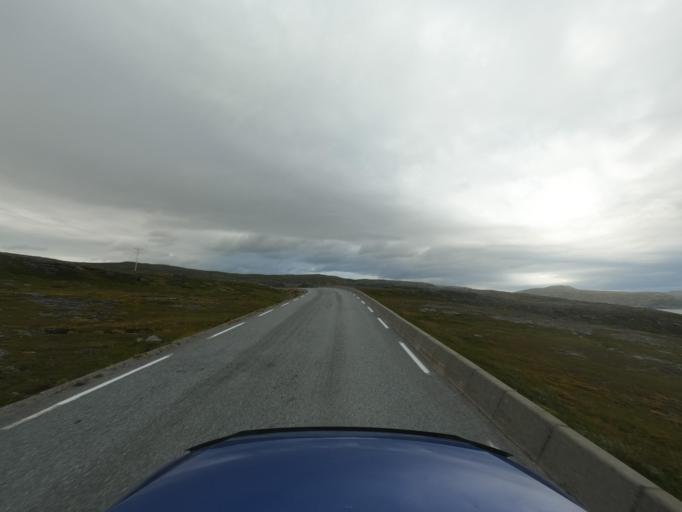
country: NO
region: Finnmark Fylke
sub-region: Nordkapp
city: Honningsvag
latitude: 70.7445
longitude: 25.6041
